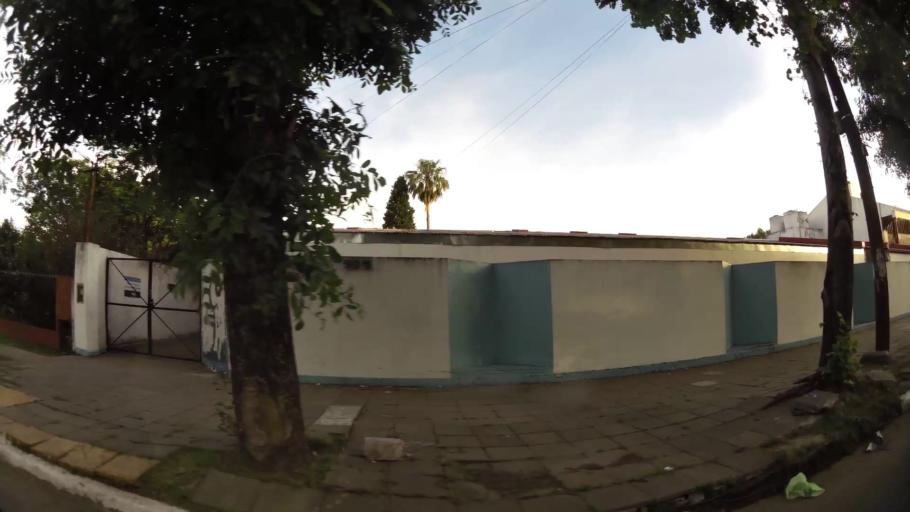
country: AR
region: Buenos Aires
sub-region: Partido de Almirante Brown
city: Adrogue
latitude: -34.7928
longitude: -58.3525
